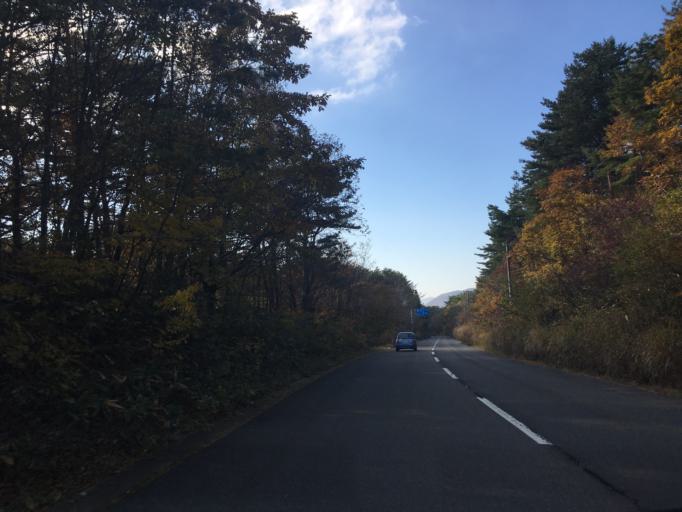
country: JP
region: Fukushima
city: Sukagawa
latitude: 37.2624
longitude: 140.1074
